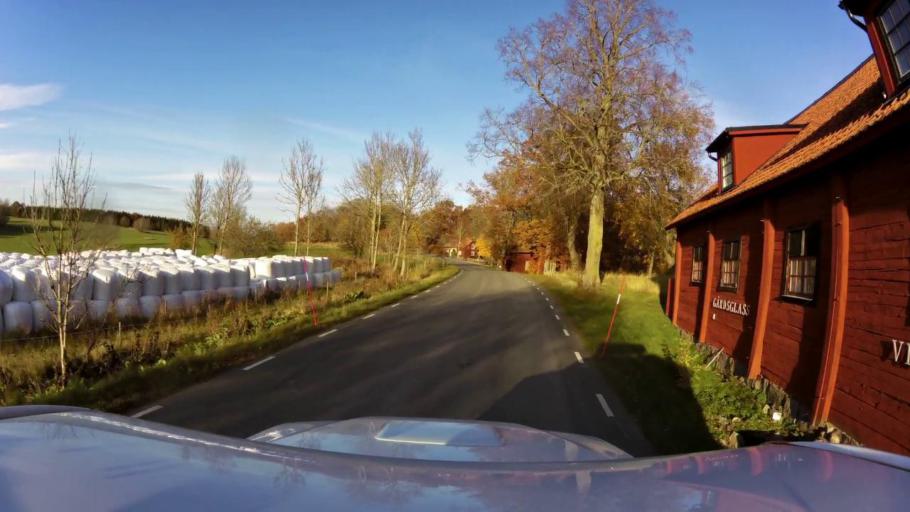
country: SE
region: OEstergoetland
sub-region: Linkopings Kommun
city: Sturefors
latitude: 58.2959
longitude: 15.6712
